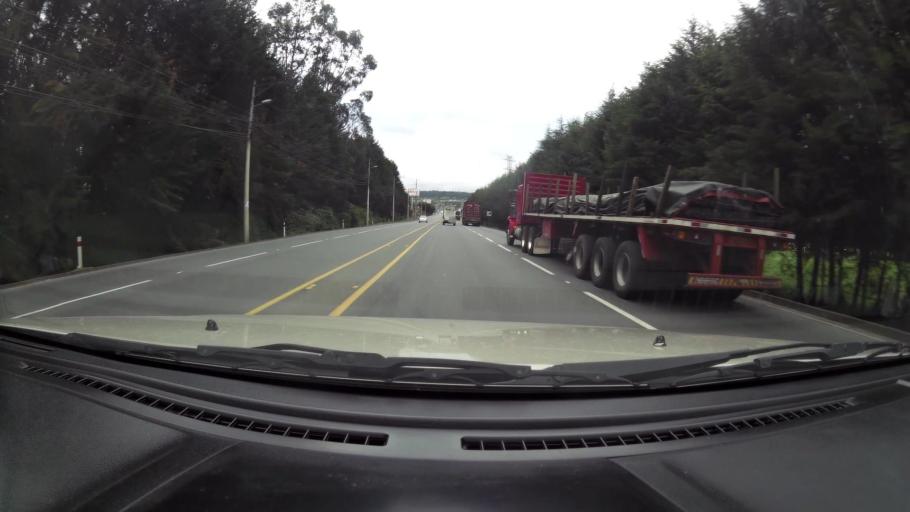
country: EC
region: Pichincha
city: Machachi
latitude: -0.4457
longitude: -78.6016
